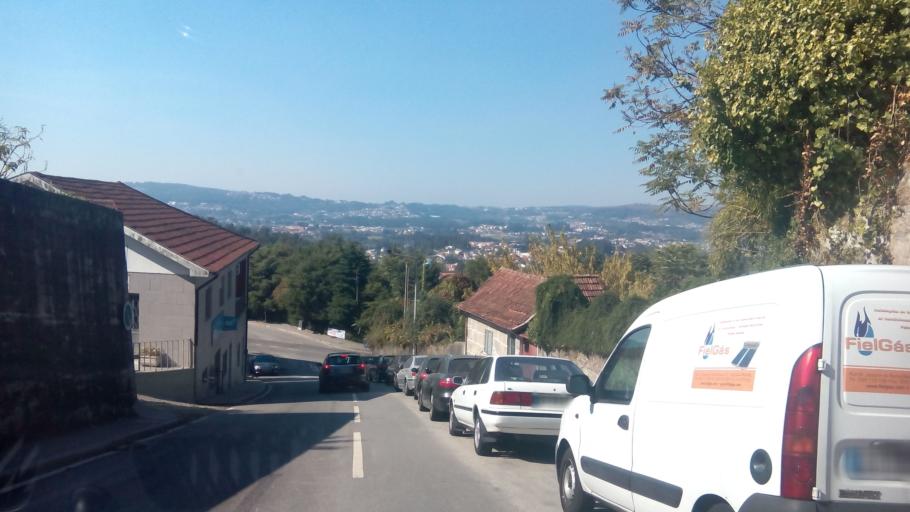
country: PT
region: Porto
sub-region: Penafiel
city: Penafiel
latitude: 41.2088
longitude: -8.2856
